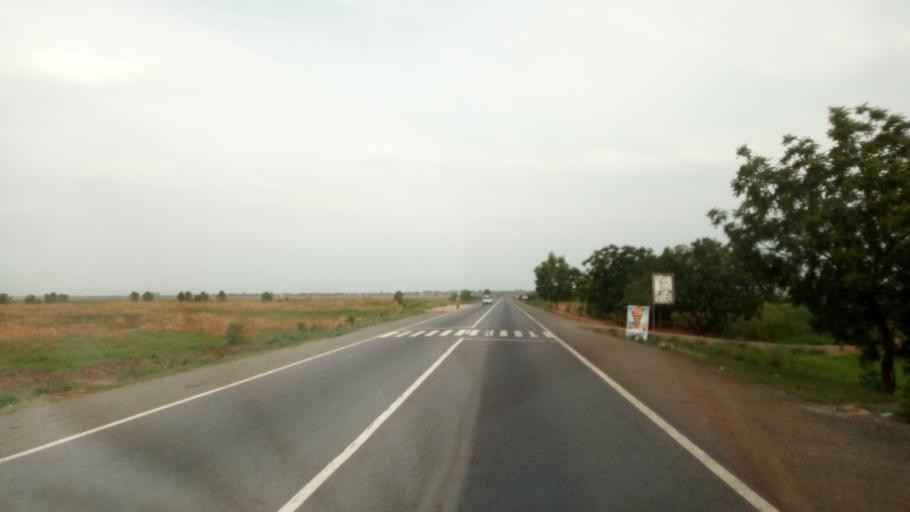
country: GH
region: Volta
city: Keta
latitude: 6.0548
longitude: 0.9638
